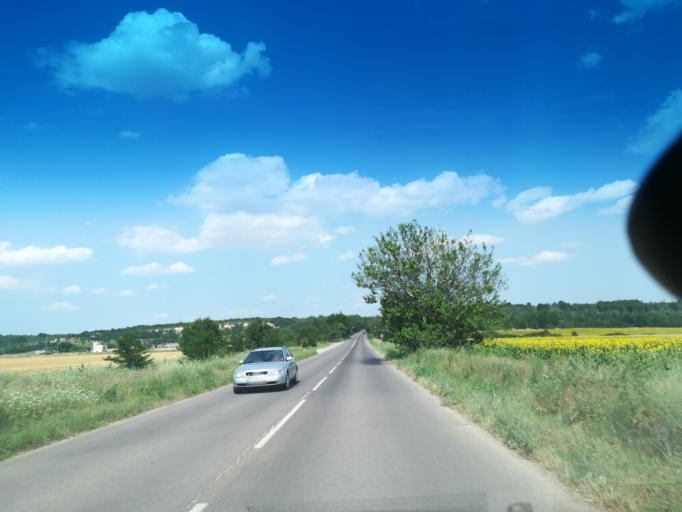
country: BG
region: Stara Zagora
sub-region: Obshtina Chirpan
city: Chirpan
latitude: 42.1785
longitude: 25.2172
